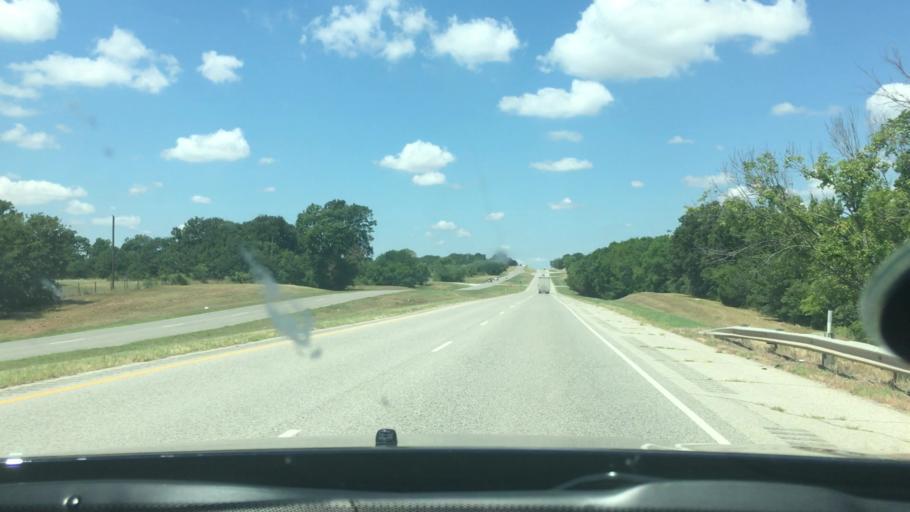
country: US
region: Oklahoma
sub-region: Carter County
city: Wilson
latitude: 34.1730
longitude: -97.3958
